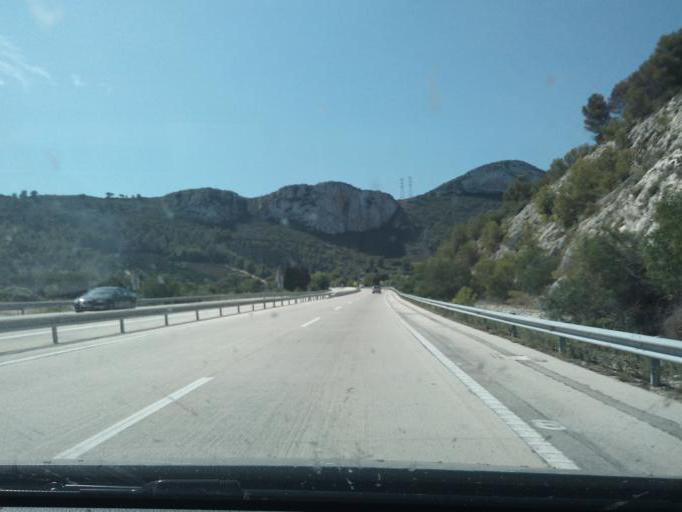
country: ES
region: Valencia
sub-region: Provincia de Valencia
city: Xeresa
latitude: 39.0097
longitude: -0.2237
